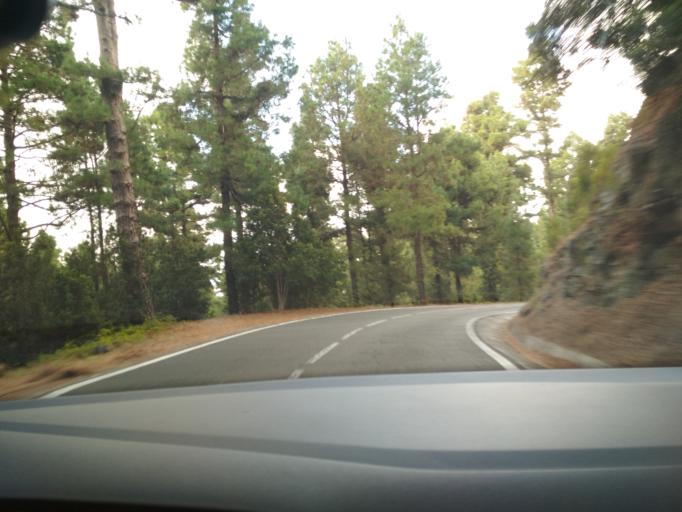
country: ES
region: Canary Islands
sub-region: Provincia de Santa Cruz de Tenerife
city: Garachico
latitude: 28.3336
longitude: -16.7563
